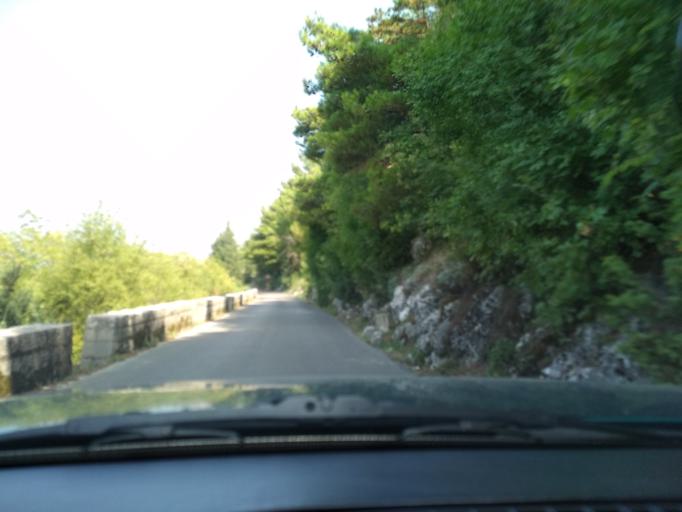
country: ME
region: Kotor
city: Kotor
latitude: 42.4053
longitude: 18.7765
